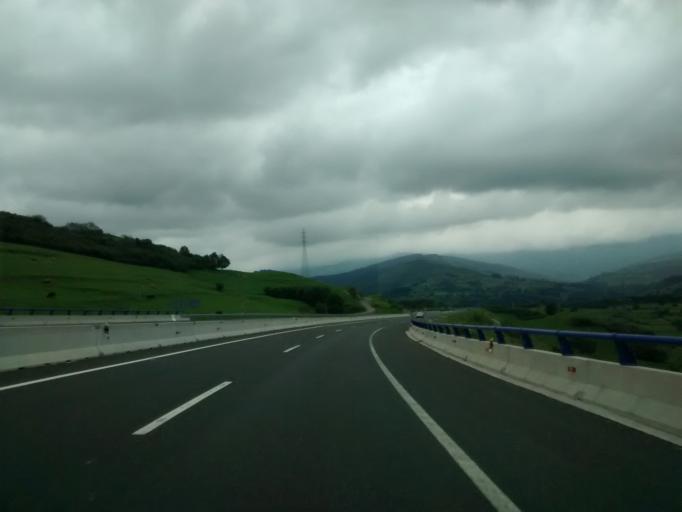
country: ES
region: Cantabria
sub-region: Provincia de Cantabria
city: Barcena de Pie de Concha
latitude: 43.1379
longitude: -4.0649
